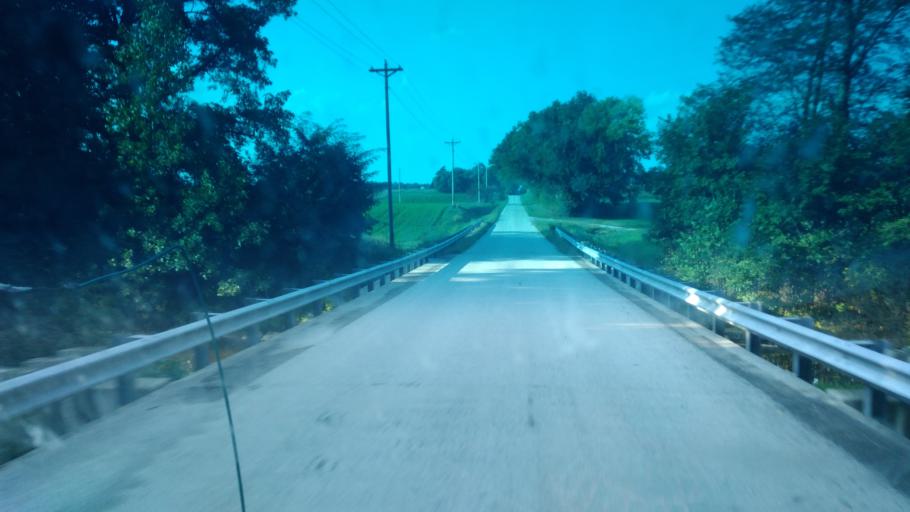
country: US
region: Ohio
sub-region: Crawford County
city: Bucyrus
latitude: 40.9316
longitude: -83.1124
